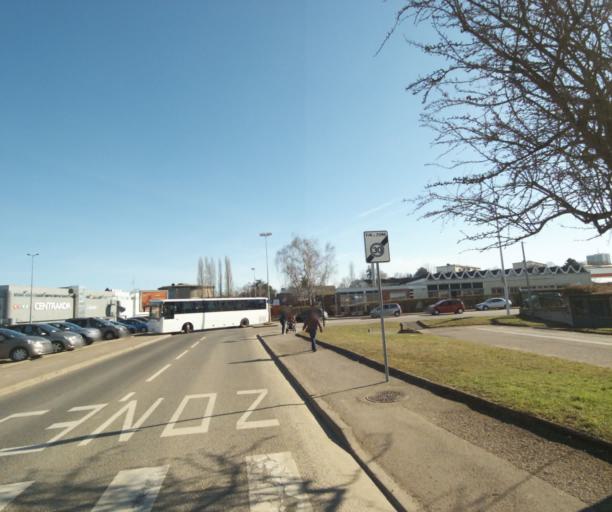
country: FR
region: Lorraine
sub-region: Departement de Meurthe-et-Moselle
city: Nancy
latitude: 48.6683
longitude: 6.1871
